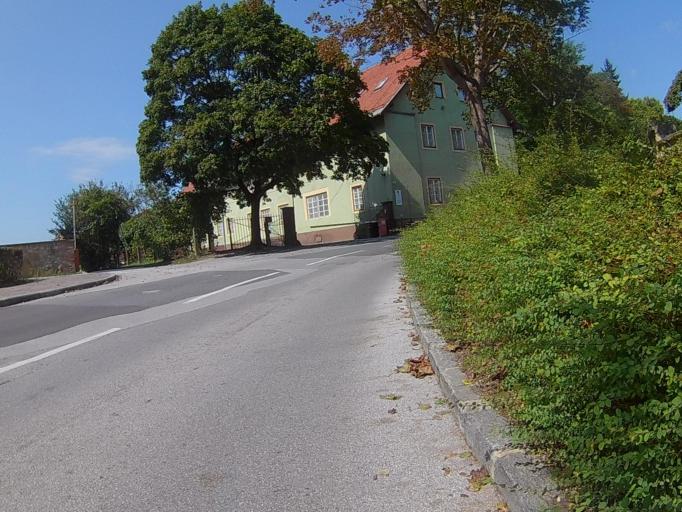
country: SI
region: Ptuj
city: Ptuj
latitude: 46.4206
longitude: 15.8654
